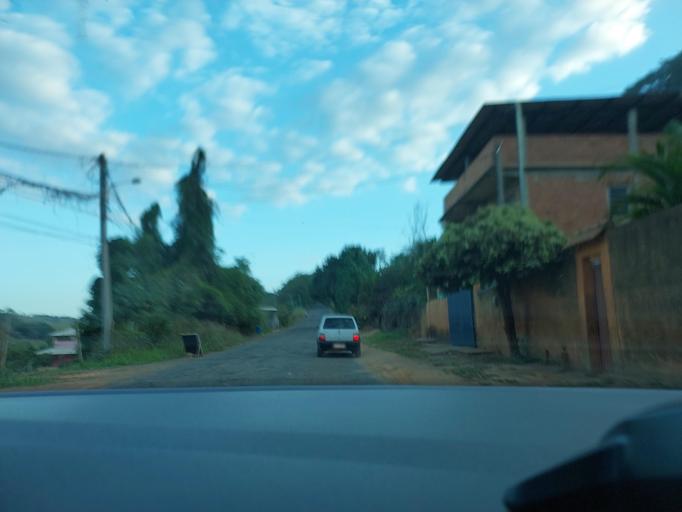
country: BR
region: Rio de Janeiro
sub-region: Natividade
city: Natividade
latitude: -21.1839
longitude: -42.1037
